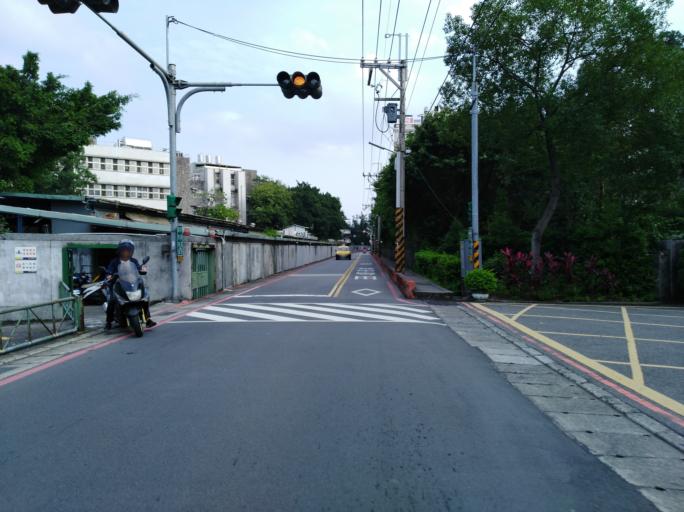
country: TW
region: Taipei
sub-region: Taipei
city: Banqiao
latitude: 25.0353
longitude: 121.4296
